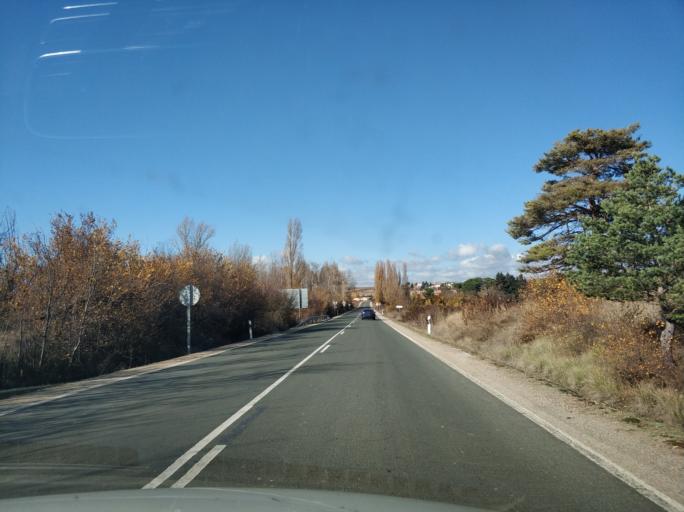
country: ES
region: Castille and Leon
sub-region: Provincia de Soria
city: Almazan
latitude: 41.4711
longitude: -2.5267
